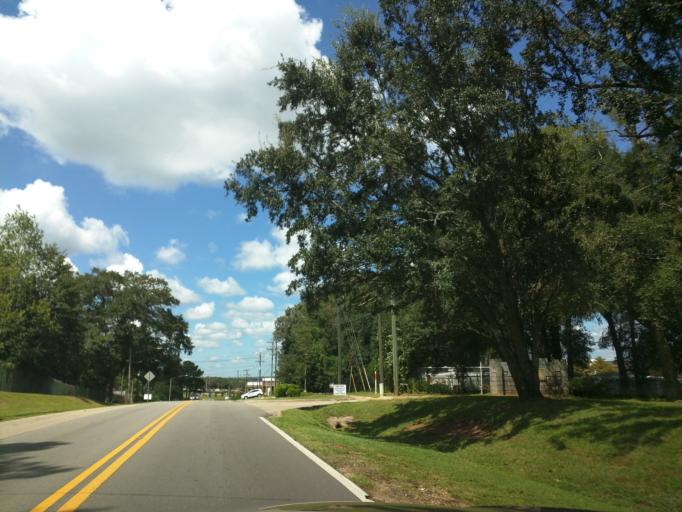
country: US
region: Florida
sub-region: Leon County
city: Tallahassee
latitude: 30.4490
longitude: -84.2200
